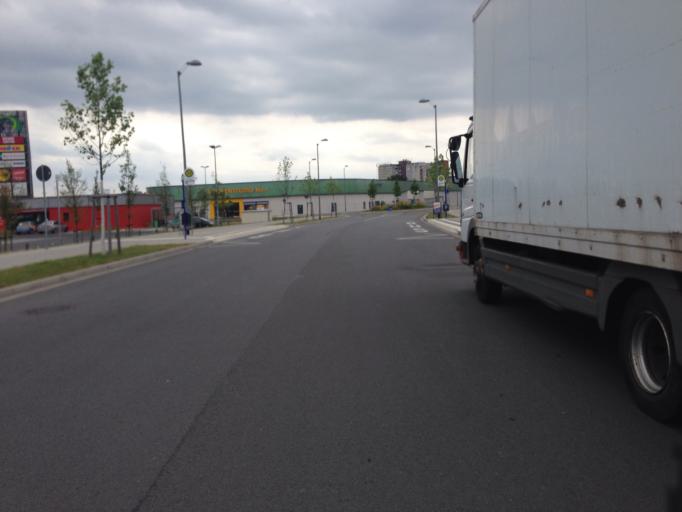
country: DE
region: Hesse
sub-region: Regierungsbezirk Darmstadt
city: Hanau am Main
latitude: 50.1474
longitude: 8.9293
